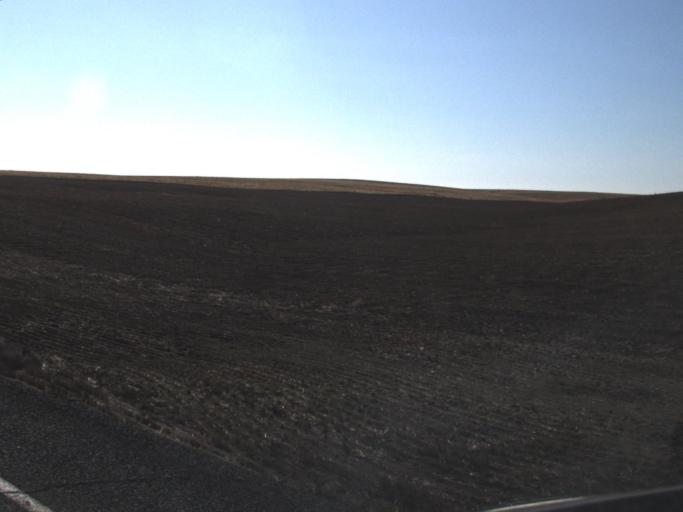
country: US
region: Washington
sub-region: Franklin County
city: Connell
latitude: 46.7483
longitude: -118.5476
